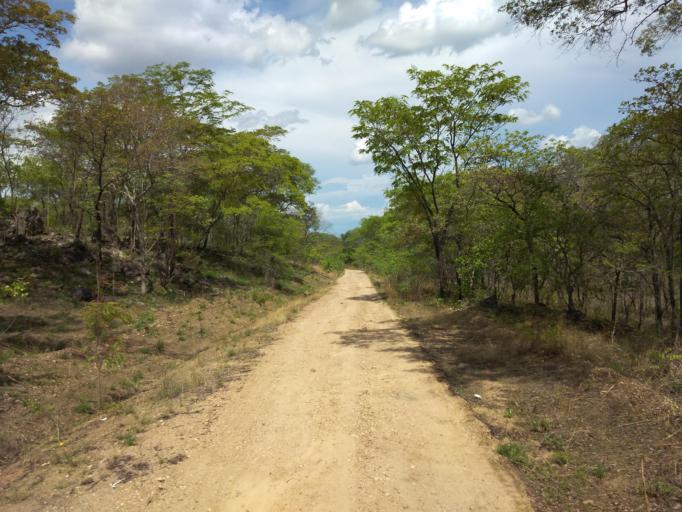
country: ZM
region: Eastern
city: Nyimba
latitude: -14.1246
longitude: 30.0917
